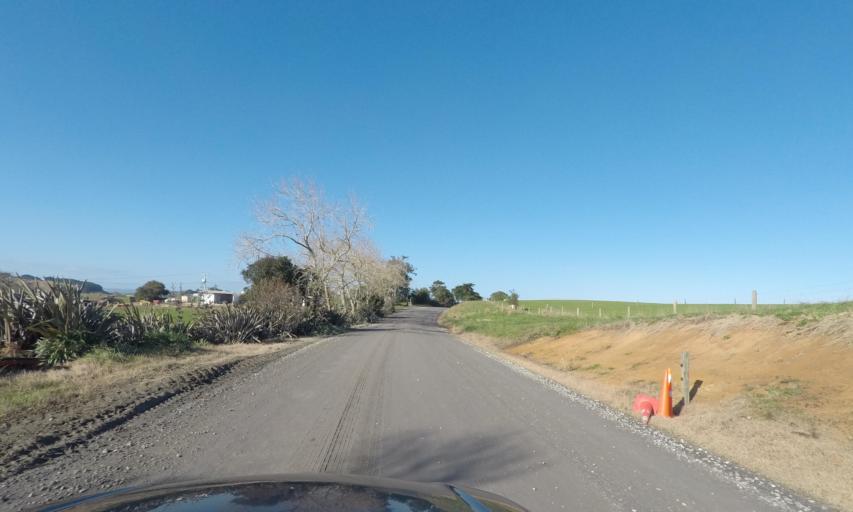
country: NZ
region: Auckland
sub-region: Auckland
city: Wellsford
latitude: -36.1552
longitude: 174.6019
